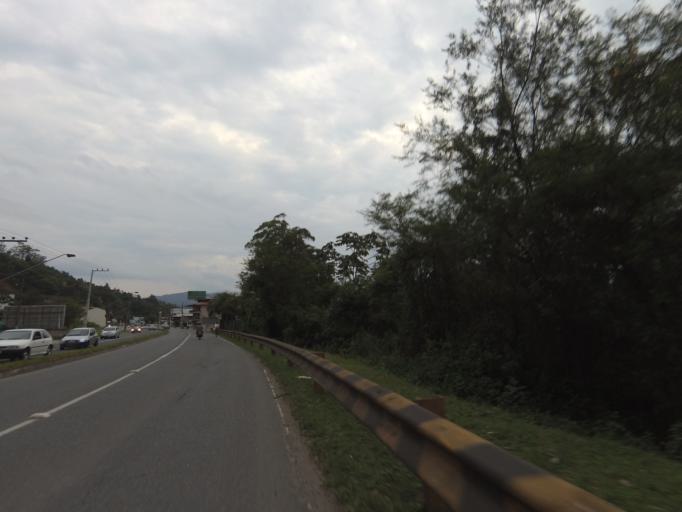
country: BR
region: Santa Catarina
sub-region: Blumenau
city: Blumenau
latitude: -26.8998
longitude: -49.0611
